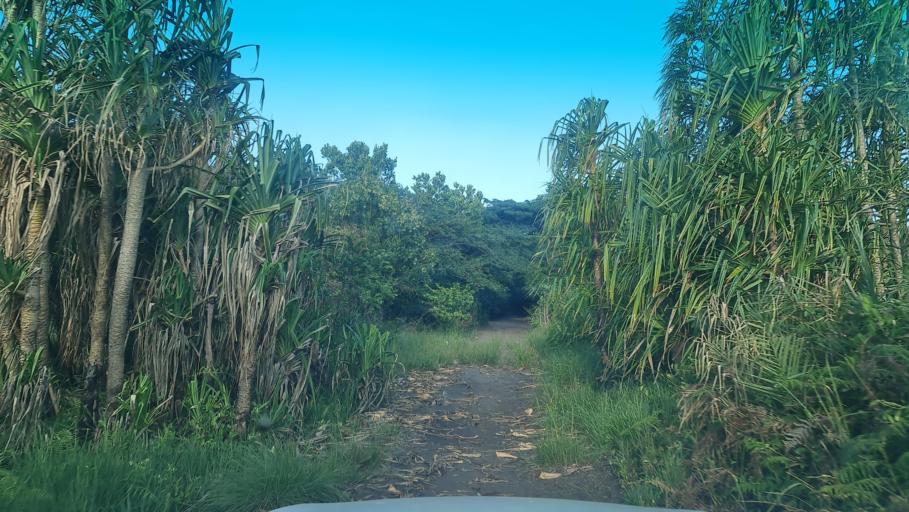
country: MZ
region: Gaza
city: Macia
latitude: -25.2281
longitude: 33.0188
